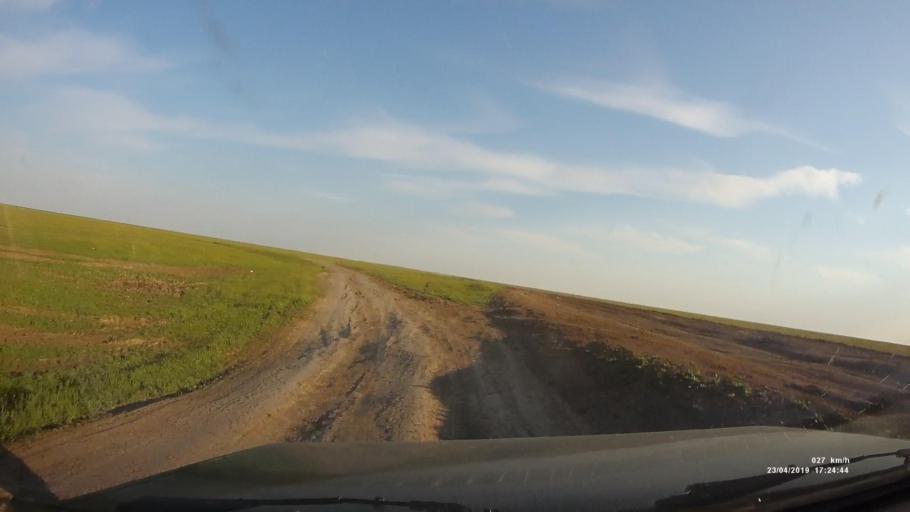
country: RU
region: Kalmykiya
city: Priyutnoye
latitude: 46.1559
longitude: 43.5089
